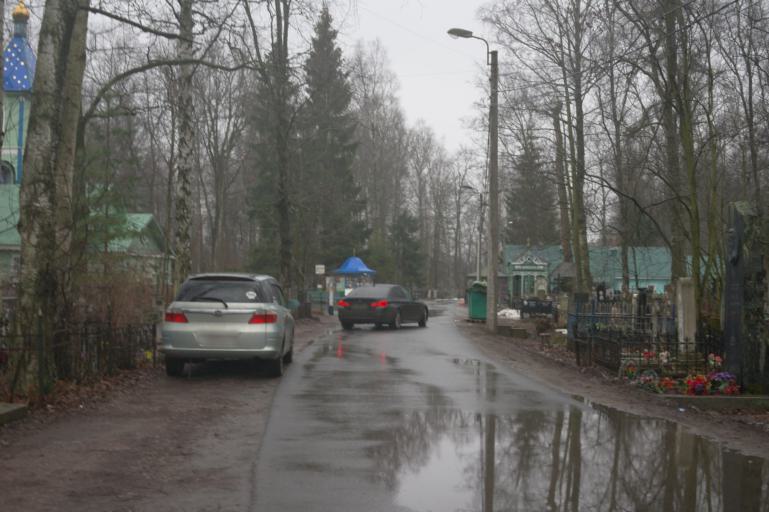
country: RU
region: St.-Petersburg
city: Komendantsky aerodrom
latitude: 59.9923
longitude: 30.2697
